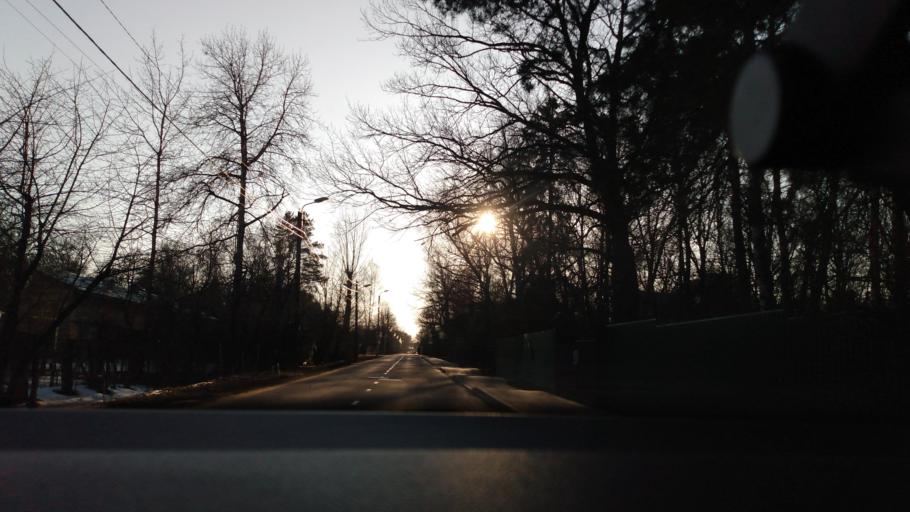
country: RU
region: Moskovskaya
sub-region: Leninskiy Rayon
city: Vnukovo
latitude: 55.6084
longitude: 37.3035
